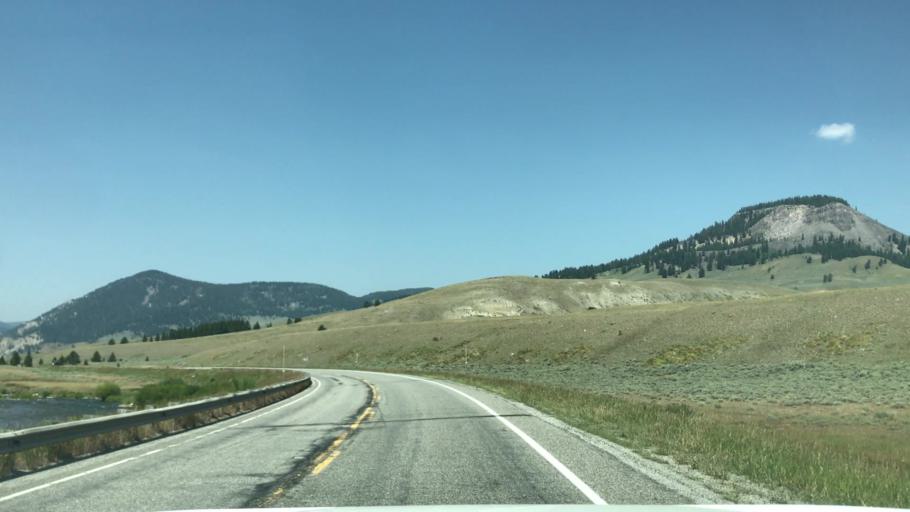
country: US
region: Montana
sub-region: Gallatin County
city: Big Sky
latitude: 45.0445
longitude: -111.1322
